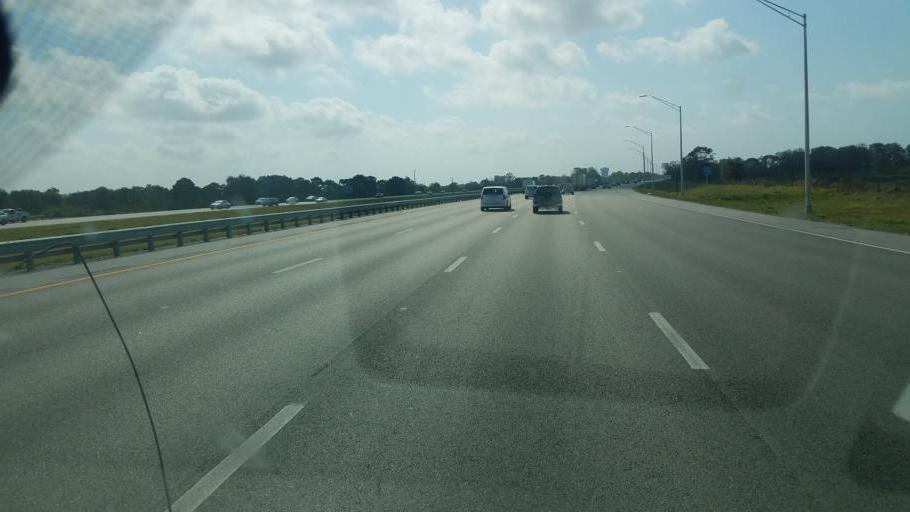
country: US
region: Florida
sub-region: Sarasota County
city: The Meadows
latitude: 27.3816
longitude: -82.4475
